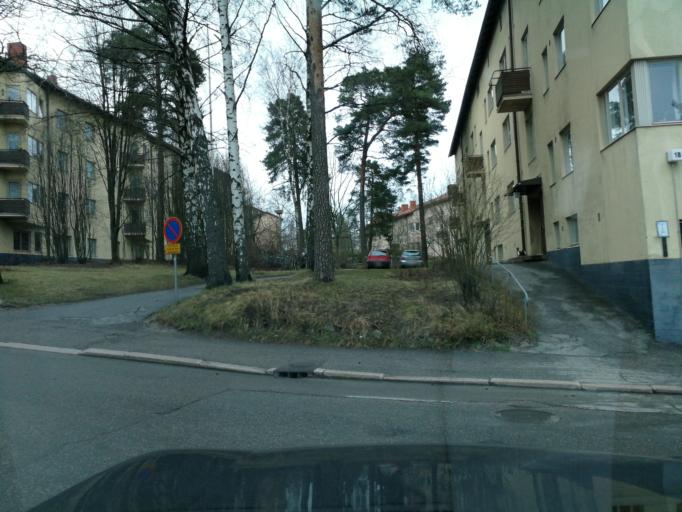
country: FI
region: Uusimaa
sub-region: Helsinki
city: Helsinki
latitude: 60.2134
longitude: 24.9562
